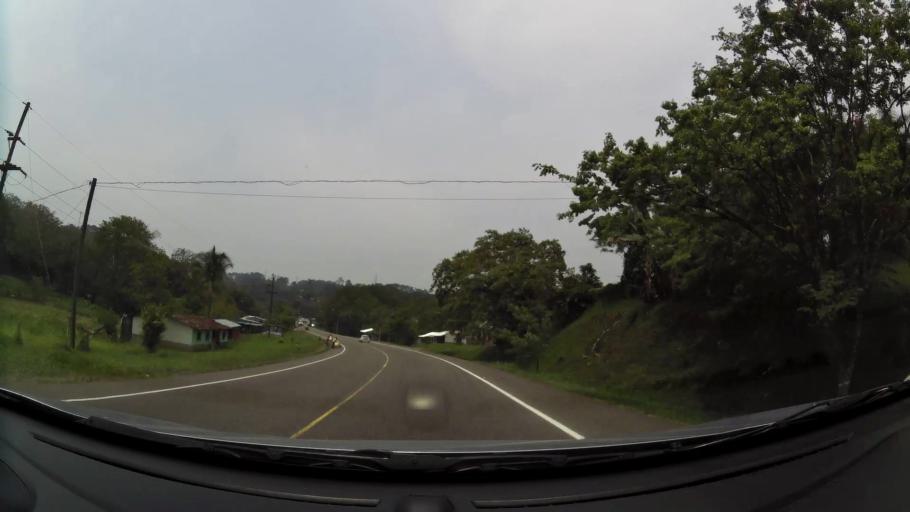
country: HN
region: Cortes
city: La Guama
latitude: 14.8813
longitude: -87.9386
